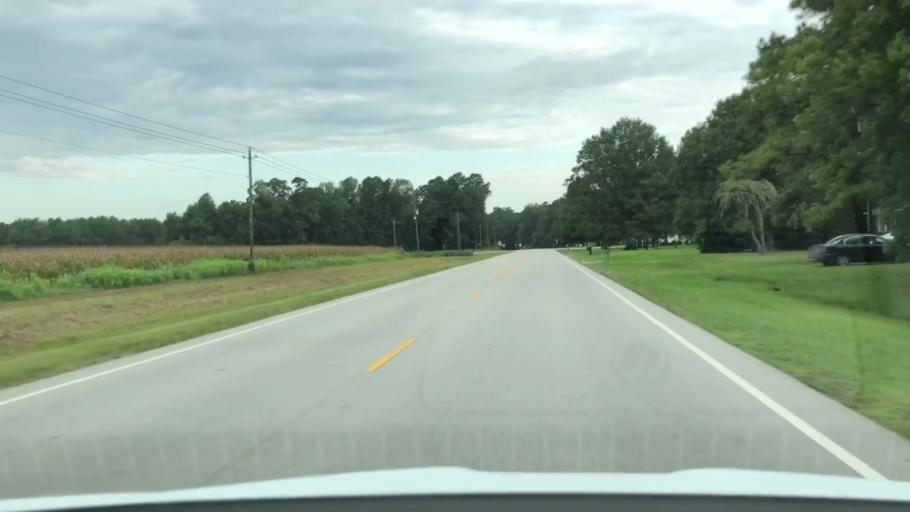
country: US
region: North Carolina
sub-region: Jones County
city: Trenton
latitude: 35.0307
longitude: -77.3140
